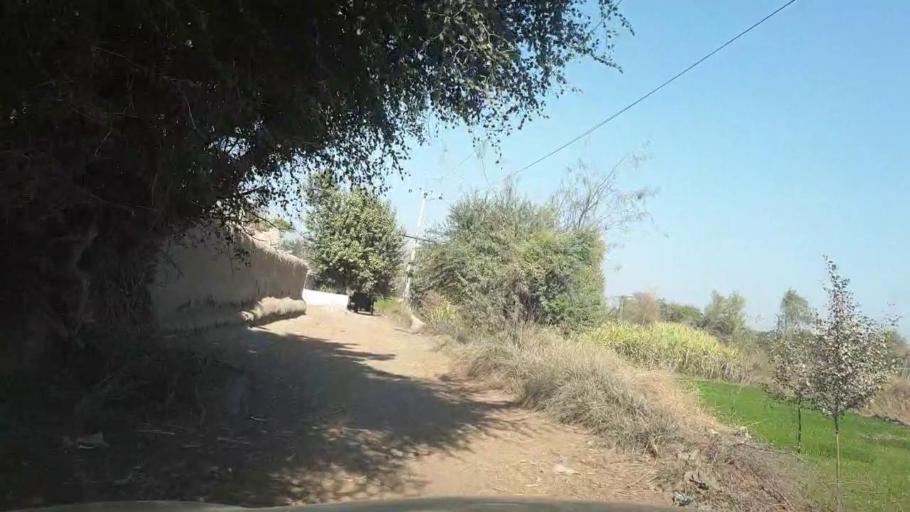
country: PK
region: Sindh
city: Adilpur
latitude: 27.9730
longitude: 69.4220
